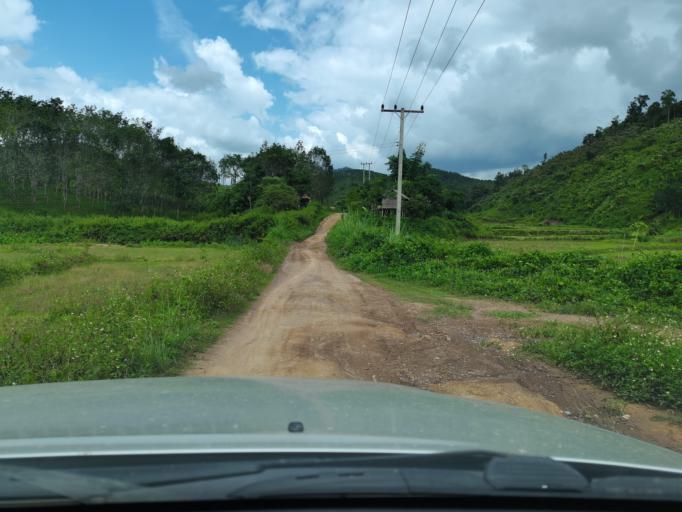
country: LA
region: Loungnamtha
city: Muang Long
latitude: 20.7006
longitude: 101.0174
